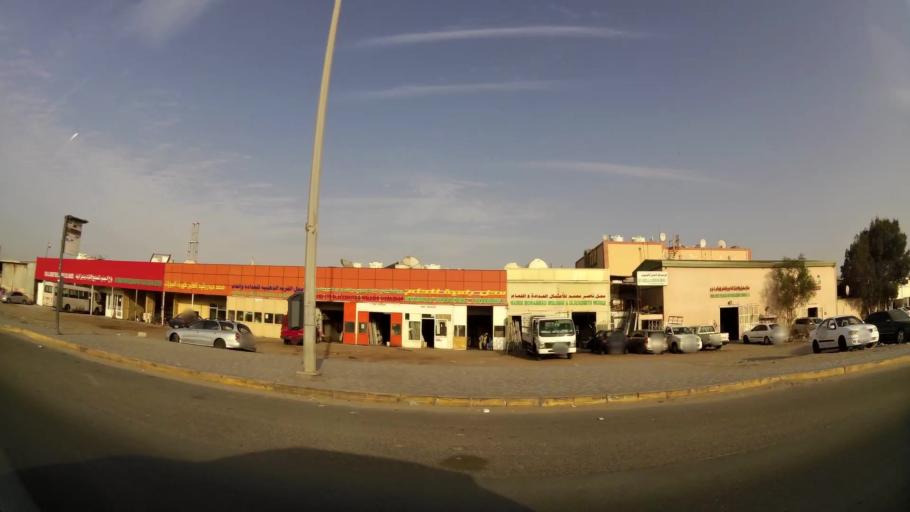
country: AE
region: Abu Dhabi
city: Abu Dhabi
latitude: 24.3711
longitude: 54.5114
